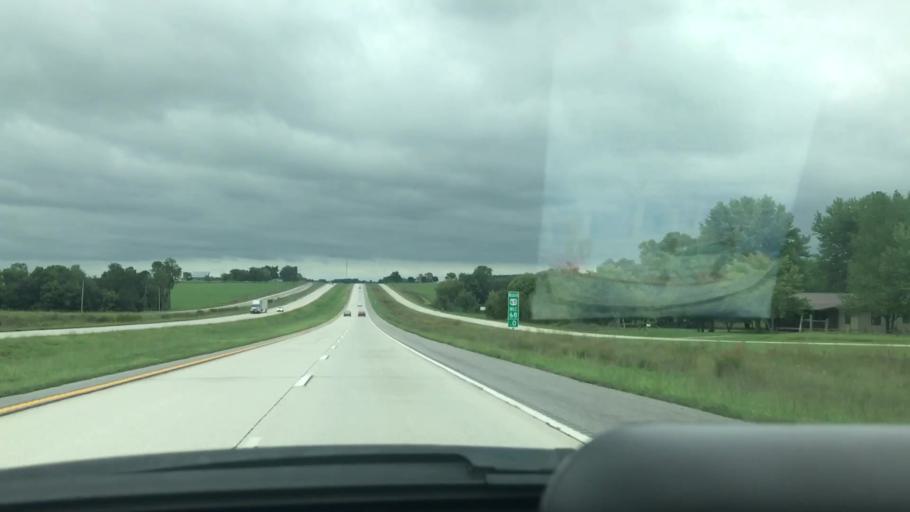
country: US
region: Missouri
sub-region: Greene County
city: Fair Grove
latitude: 37.4281
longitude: -93.1449
